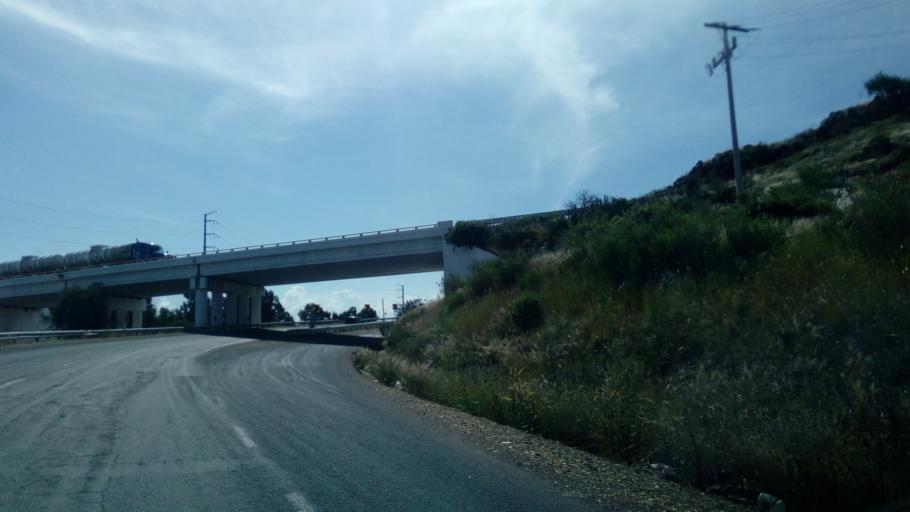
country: MX
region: Durango
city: Victoria de Durango
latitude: 24.0700
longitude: -104.6550
